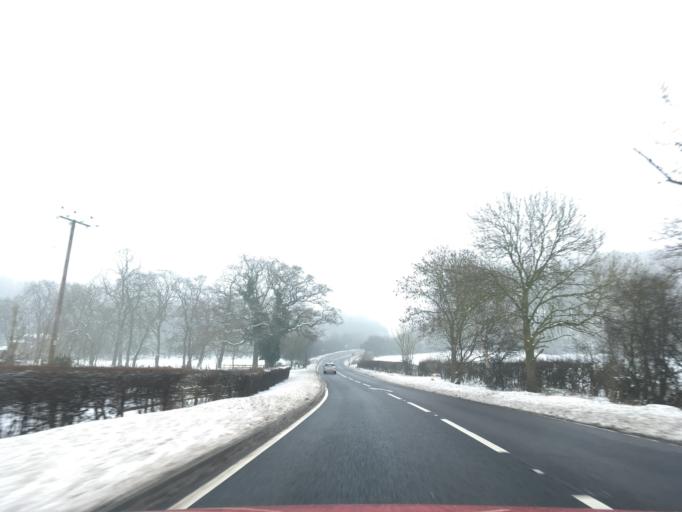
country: GB
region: England
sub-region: Warwickshire
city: Alcester
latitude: 52.2048
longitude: -1.8070
